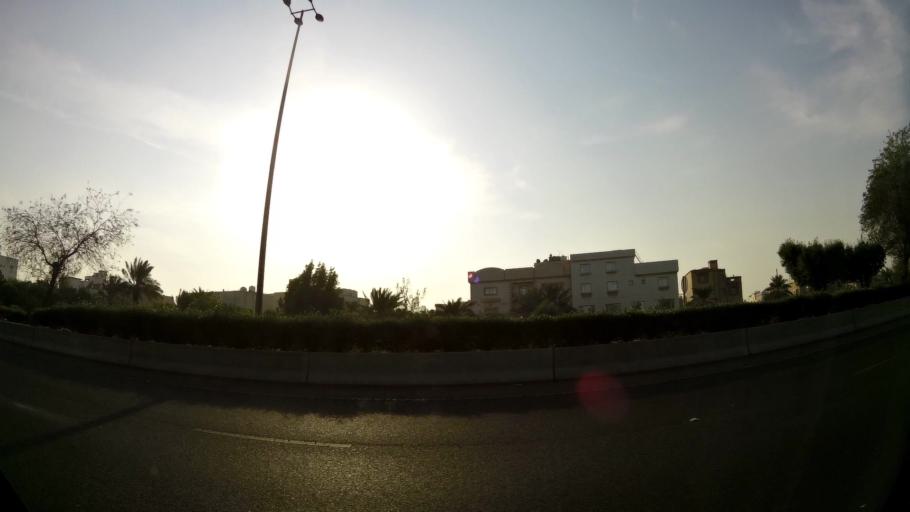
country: KW
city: Al Funaytis
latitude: 29.2149
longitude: 48.0891
